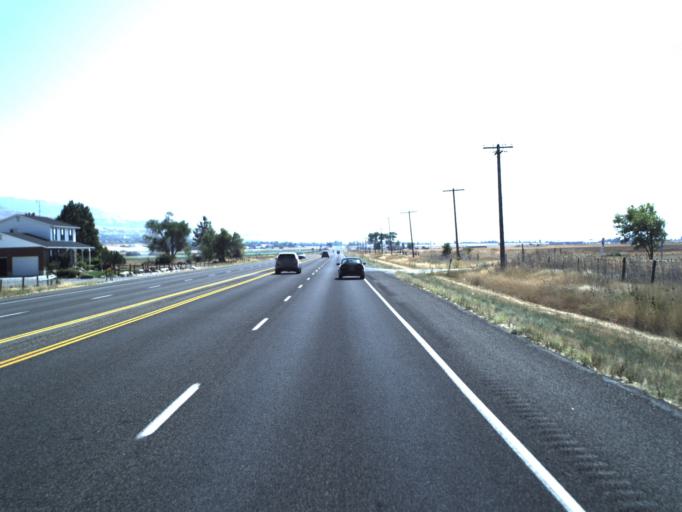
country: US
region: Utah
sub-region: Cache County
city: Lewiston
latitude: 41.9948
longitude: -111.8129
